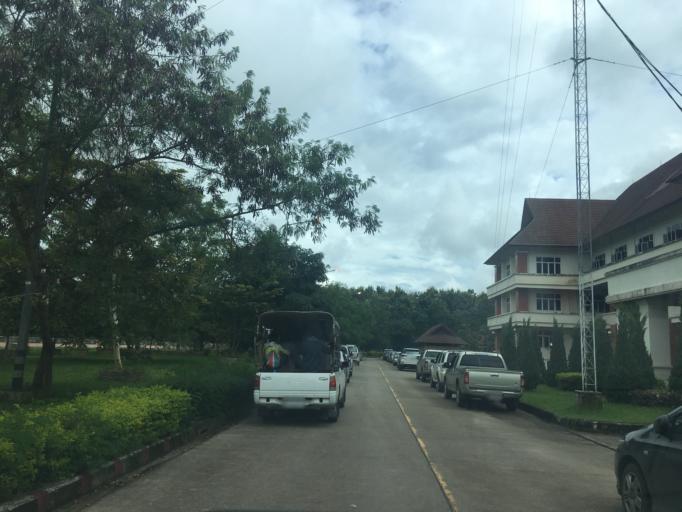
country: TH
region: Chiang Rai
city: Chiang Rai
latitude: 19.9201
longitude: 99.8134
